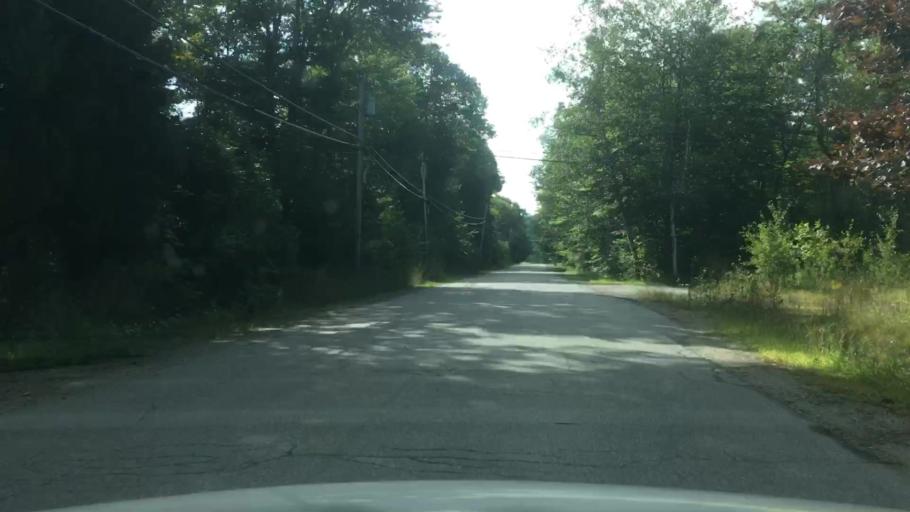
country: US
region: Maine
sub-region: Kennebec County
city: Gardiner
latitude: 44.1782
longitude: -69.8240
